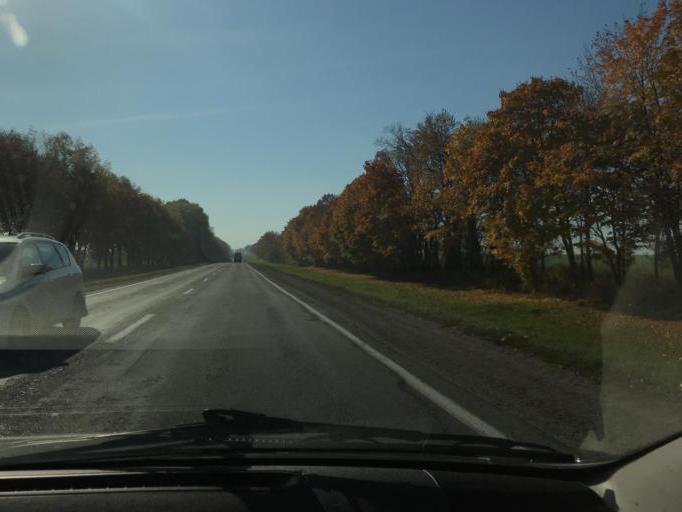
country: BY
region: Minsk
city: Salihorsk
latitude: 52.8892
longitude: 27.4716
